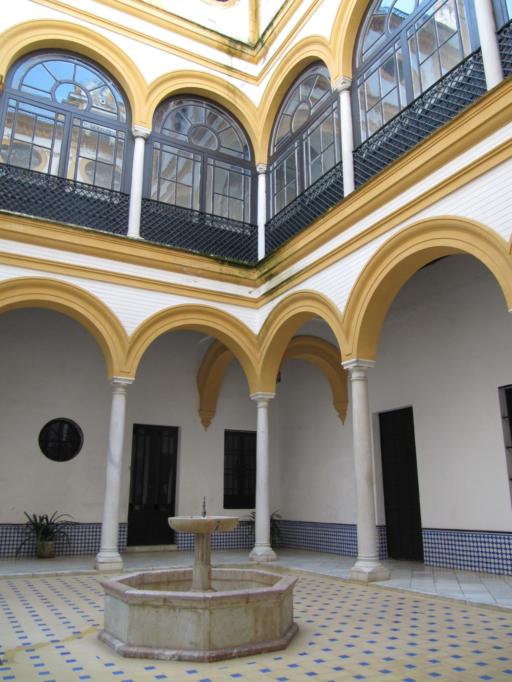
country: ES
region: Andalusia
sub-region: Provincia de Sevilla
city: Sevilla
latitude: 37.3839
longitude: -5.9916
